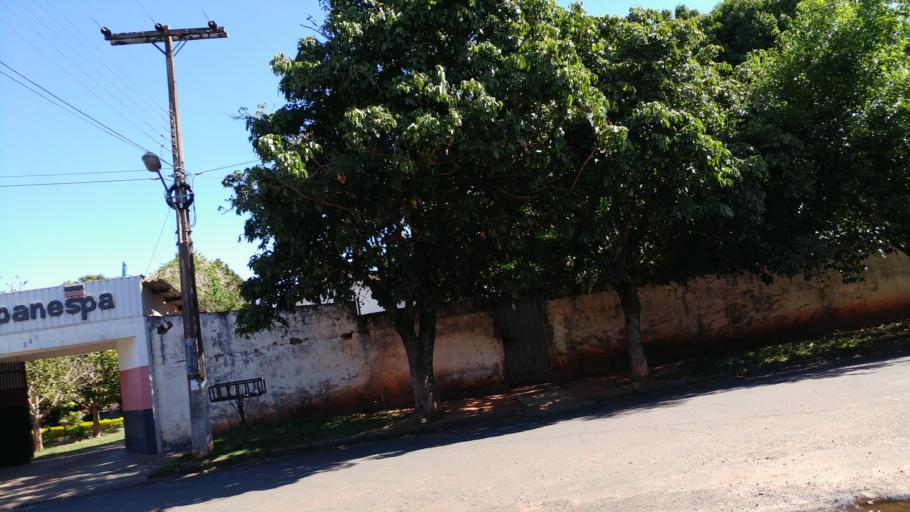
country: BR
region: Sao Paulo
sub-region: Paraguacu Paulista
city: Paraguacu Paulista
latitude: -22.4350
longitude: -50.5838
